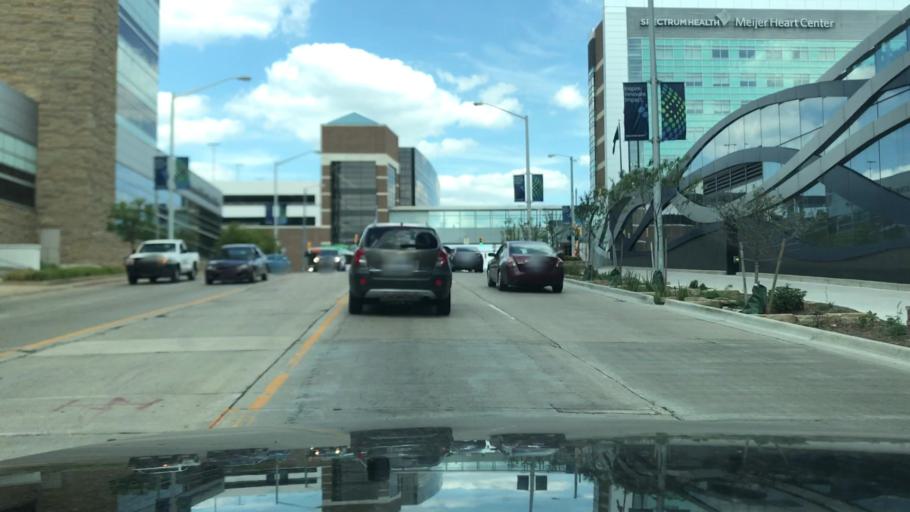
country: US
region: Michigan
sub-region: Kent County
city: Grand Rapids
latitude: 42.9705
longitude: -85.6659
